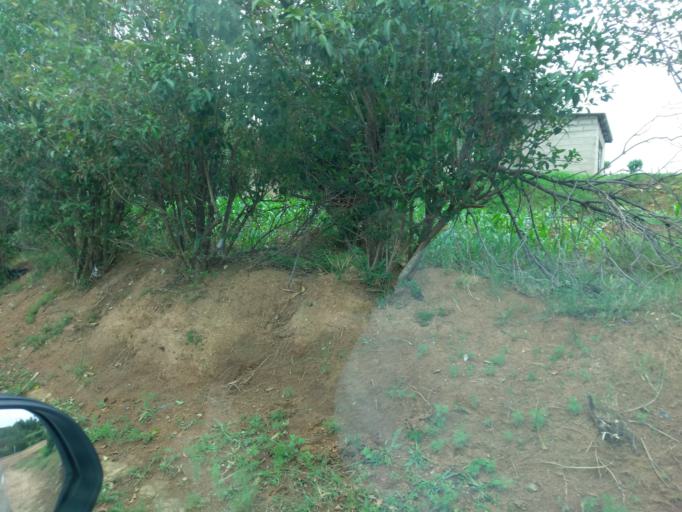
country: LS
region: Berea
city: Teyateyaneng
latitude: -29.1188
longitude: 27.9657
